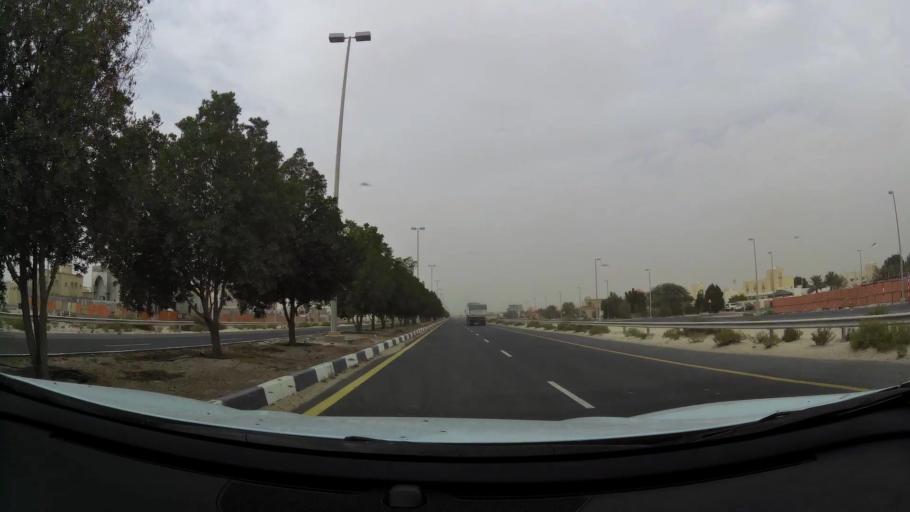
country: AE
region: Abu Dhabi
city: Abu Dhabi
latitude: 24.3649
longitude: 54.7110
